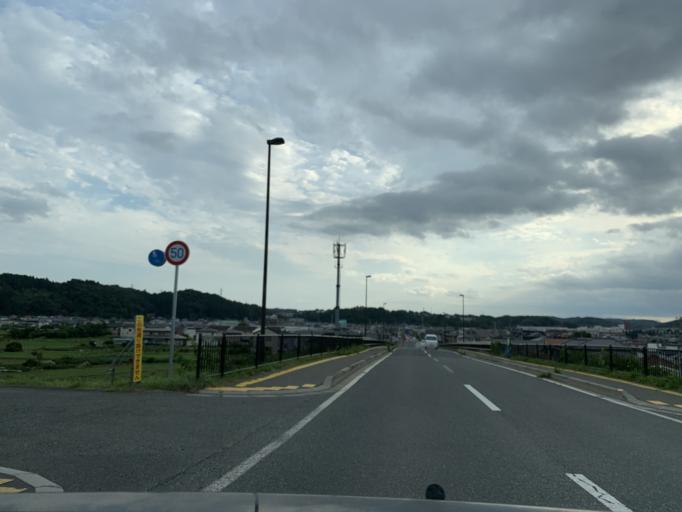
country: JP
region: Iwate
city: Ichinoseki
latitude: 38.9340
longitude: 141.1490
